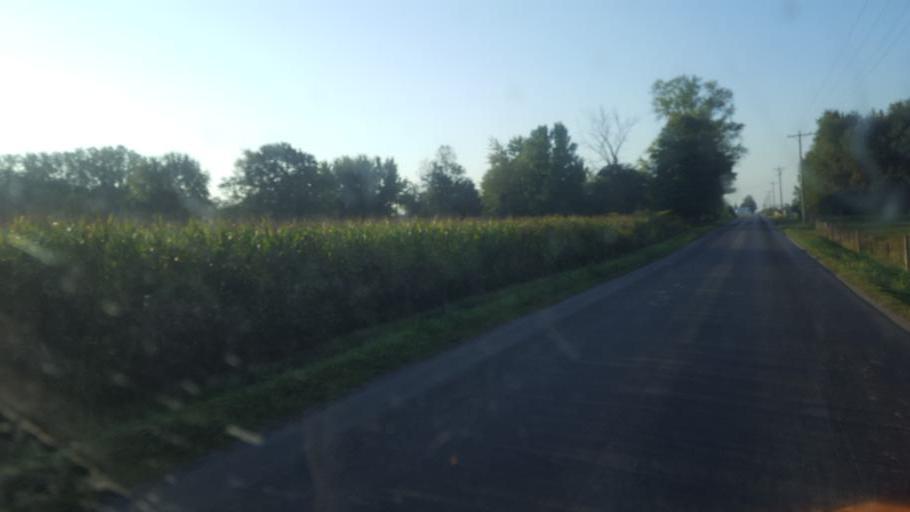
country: US
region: Indiana
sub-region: LaGrange County
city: Lagrange
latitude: 41.6063
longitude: -85.4242
